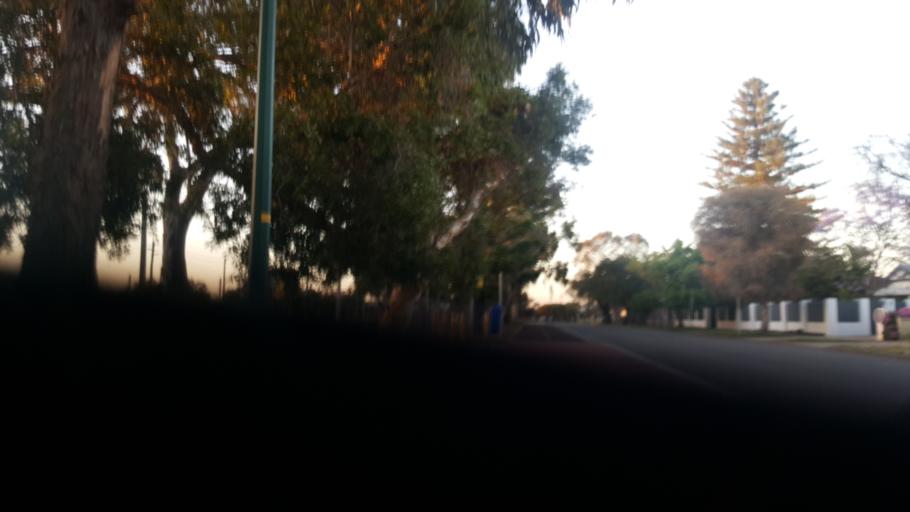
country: AU
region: Western Australia
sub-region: Victoria Park
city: East Victoria Park
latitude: -31.9865
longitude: 115.9159
